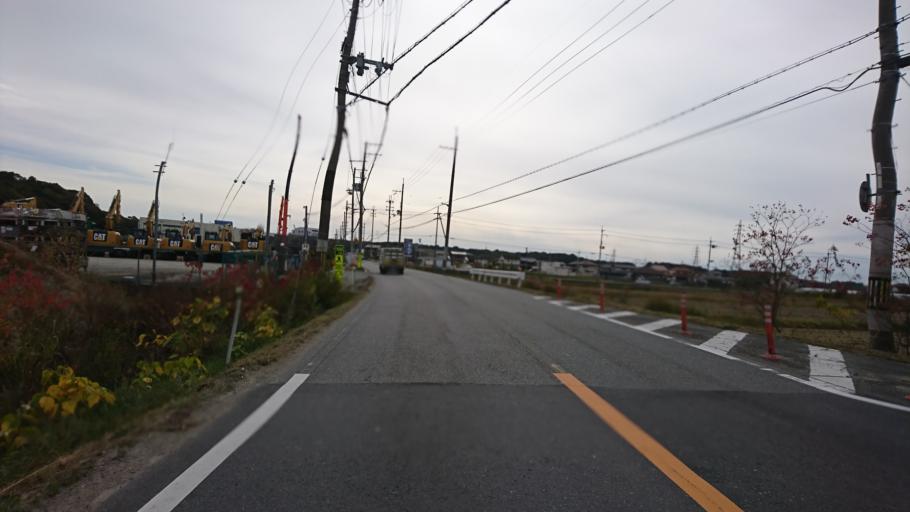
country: JP
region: Hyogo
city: Ono
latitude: 34.7908
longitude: 134.9214
